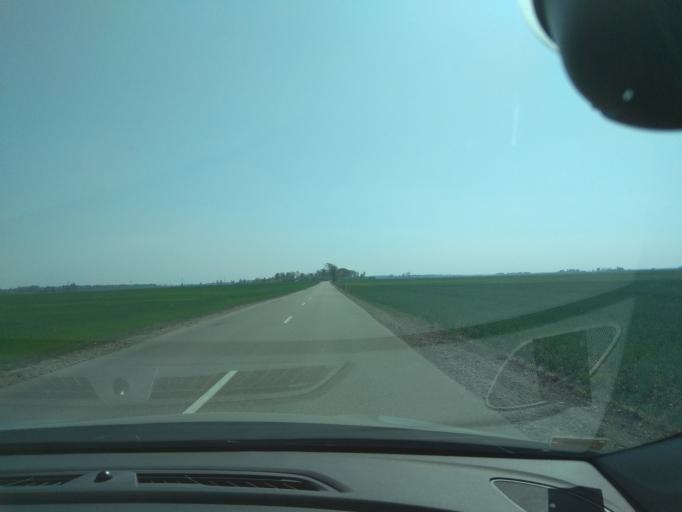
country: LT
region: Panevezys
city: Pasvalys
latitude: 55.9550
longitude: 24.2121
